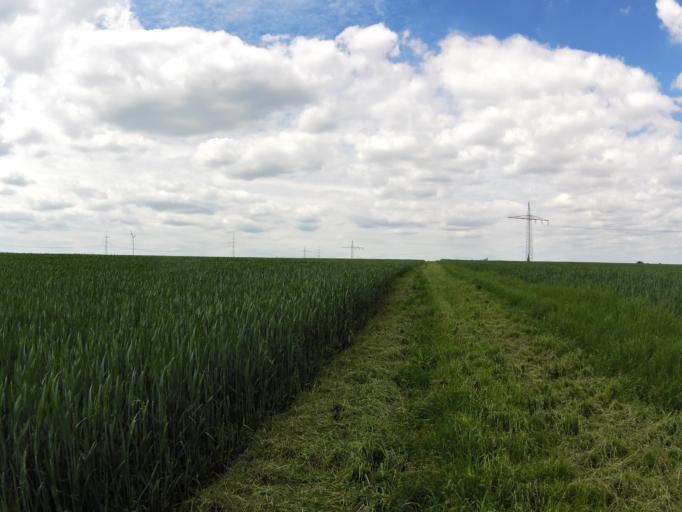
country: DE
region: Bavaria
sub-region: Regierungsbezirk Unterfranken
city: Theilheim
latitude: 49.7357
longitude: 10.0620
